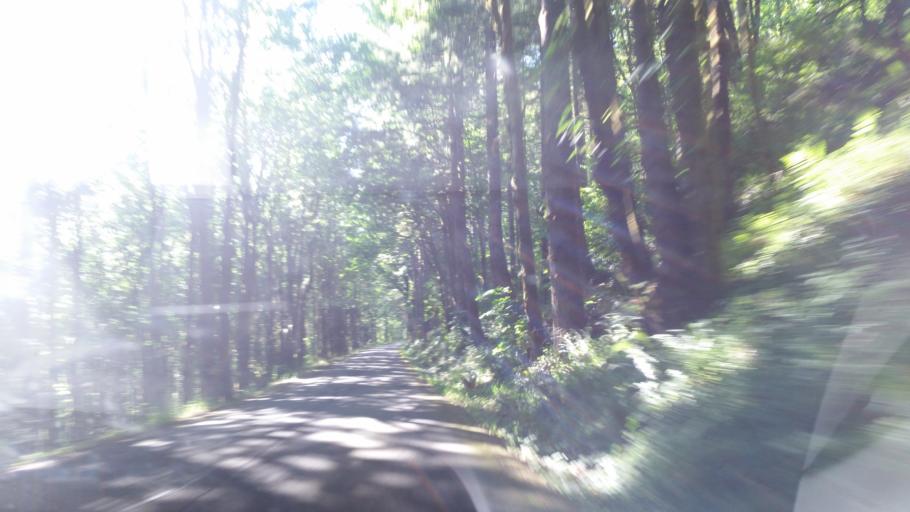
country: US
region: Washington
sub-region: Snohomish County
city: Gold Bar
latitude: 47.8225
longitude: -121.6080
